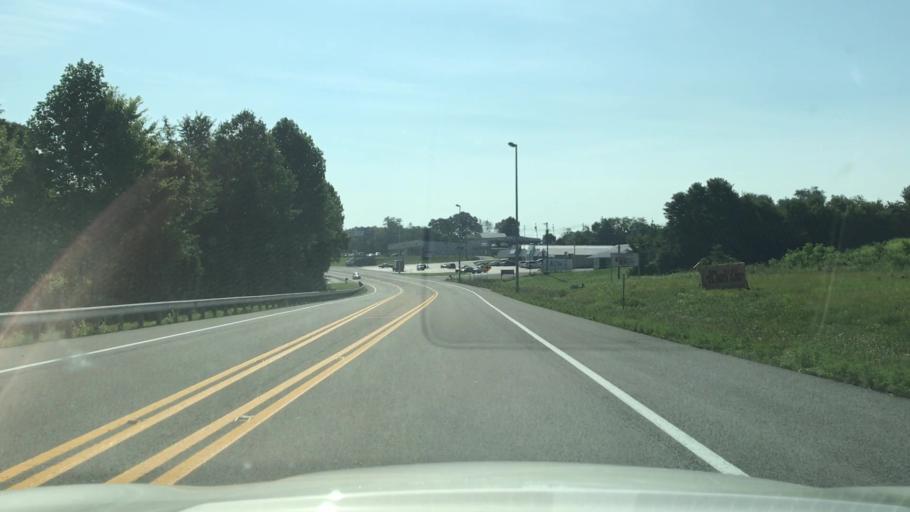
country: US
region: Tennessee
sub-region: Pickett County
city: Byrdstown
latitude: 36.5732
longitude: -85.1497
